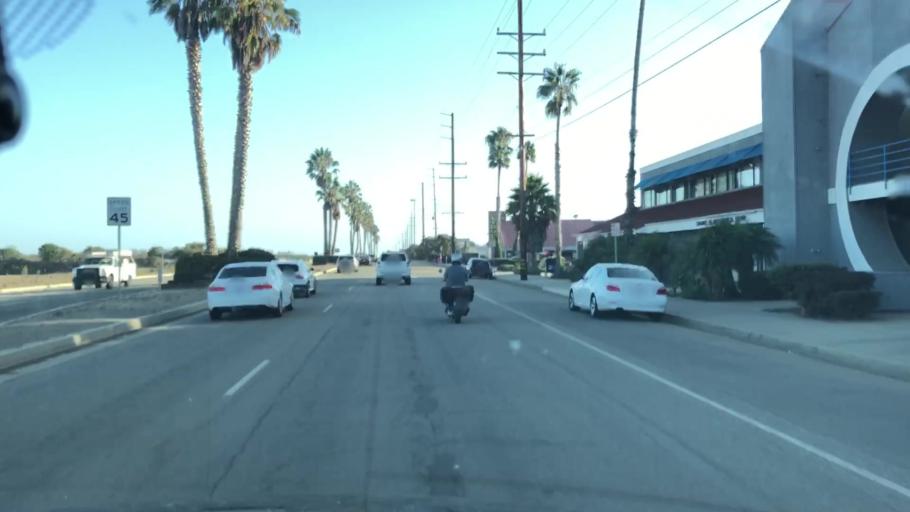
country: US
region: California
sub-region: Ventura County
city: Ventura
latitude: 34.2434
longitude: -119.2569
